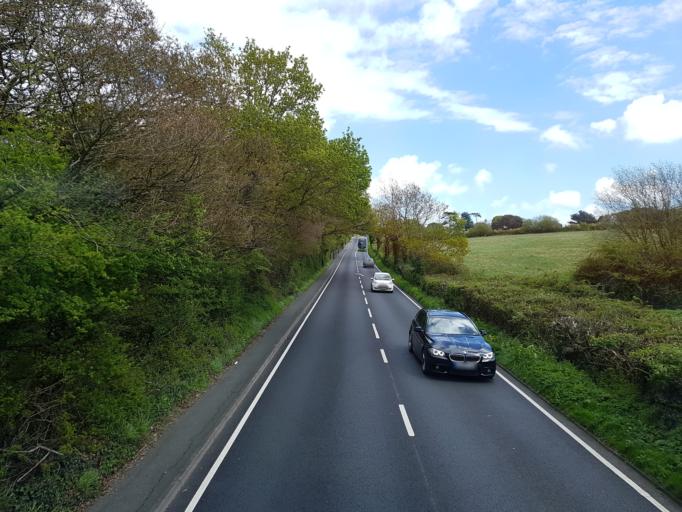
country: GB
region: England
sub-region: Isle of Wight
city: Ryde
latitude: 50.7275
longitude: -1.1979
